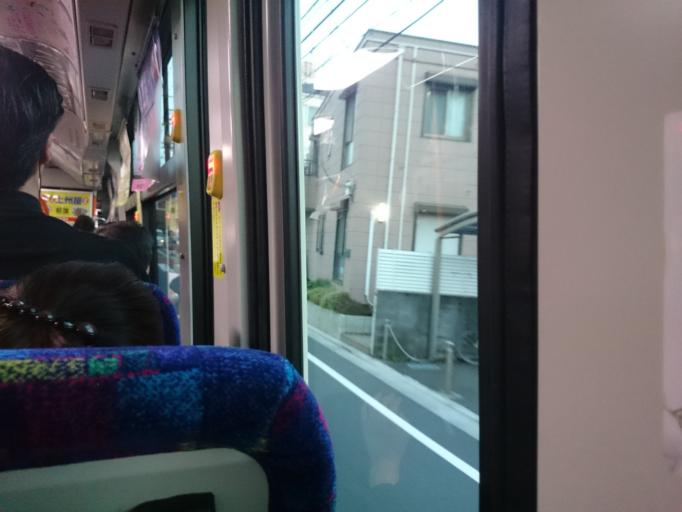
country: JP
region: Tokyo
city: Mitaka-shi
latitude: 35.6950
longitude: 139.6188
